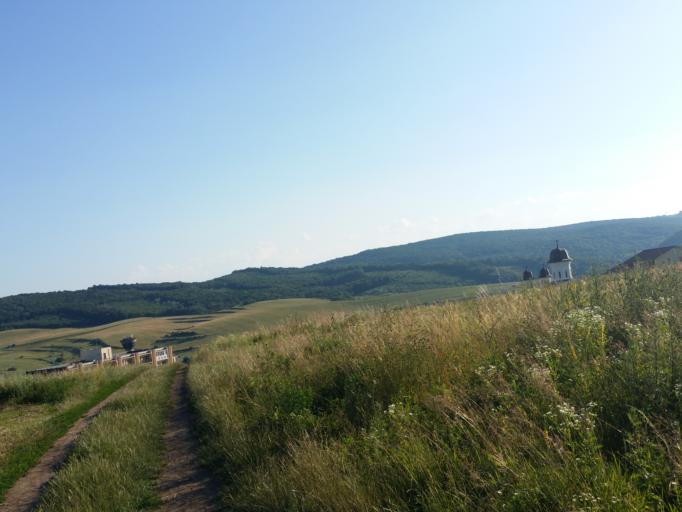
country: RO
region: Cluj
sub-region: Comuna Baciu
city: Baciu
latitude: 46.7878
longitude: 23.5413
